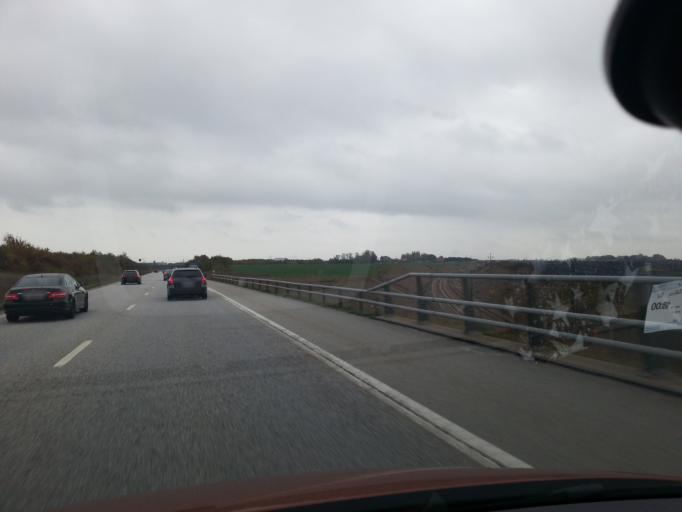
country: SE
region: Skane
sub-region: Malmo
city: Tygelsjo
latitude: 55.5479
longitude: 13.0208
